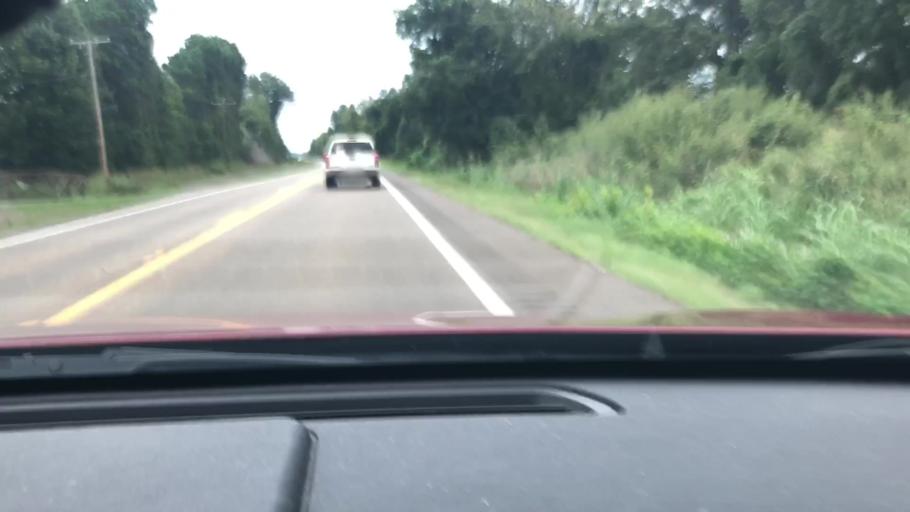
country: US
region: Arkansas
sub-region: Lafayette County
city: Lewisville
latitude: 33.3548
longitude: -93.6692
